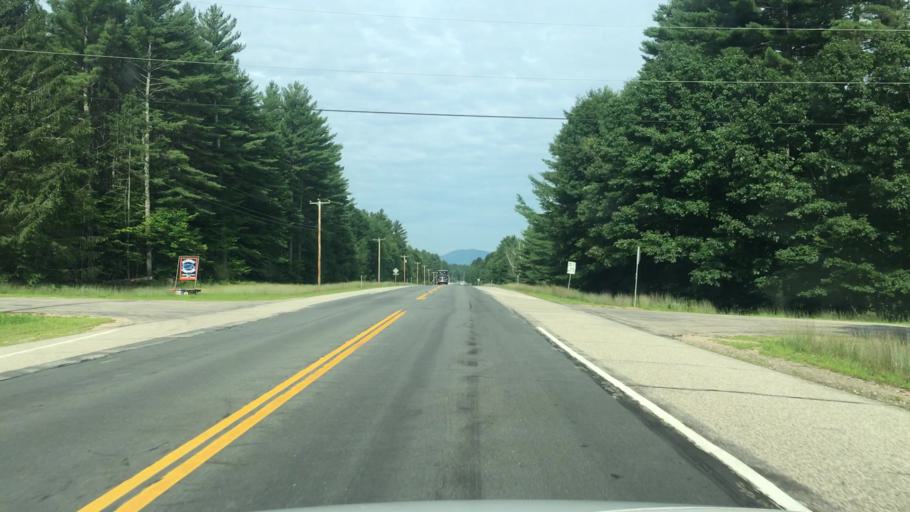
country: US
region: New Hampshire
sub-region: Carroll County
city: Tamworth
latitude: 43.8245
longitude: -71.2297
